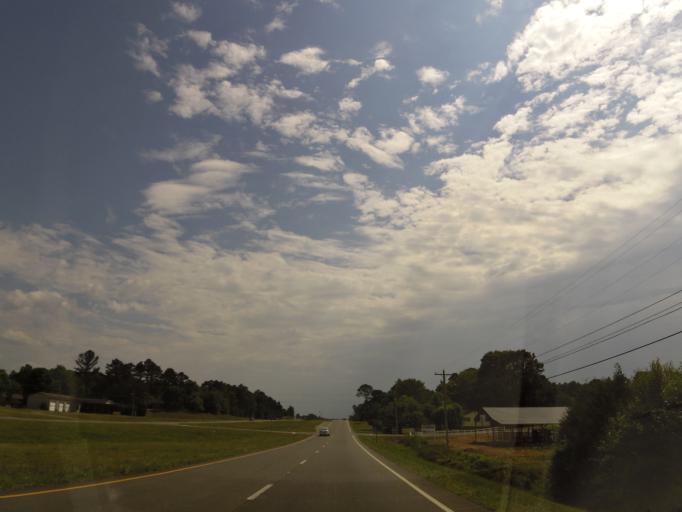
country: US
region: Alabama
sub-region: Jackson County
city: Stevenson
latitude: 34.7874
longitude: -85.8839
